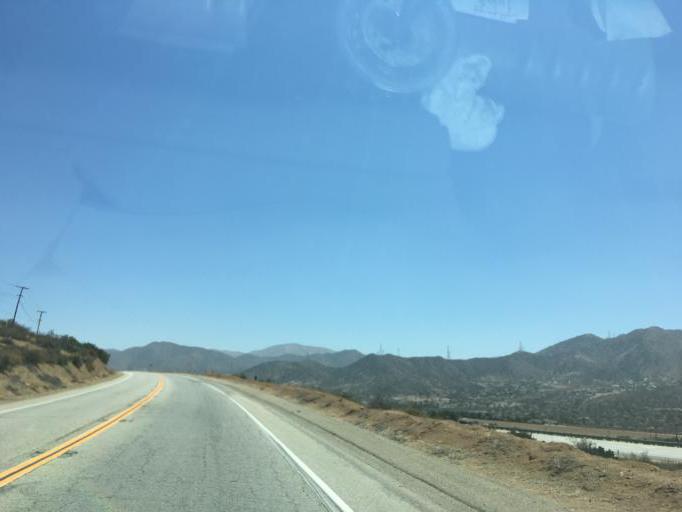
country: US
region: California
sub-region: Los Angeles County
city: Vincent
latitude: 34.4864
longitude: -118.1538
